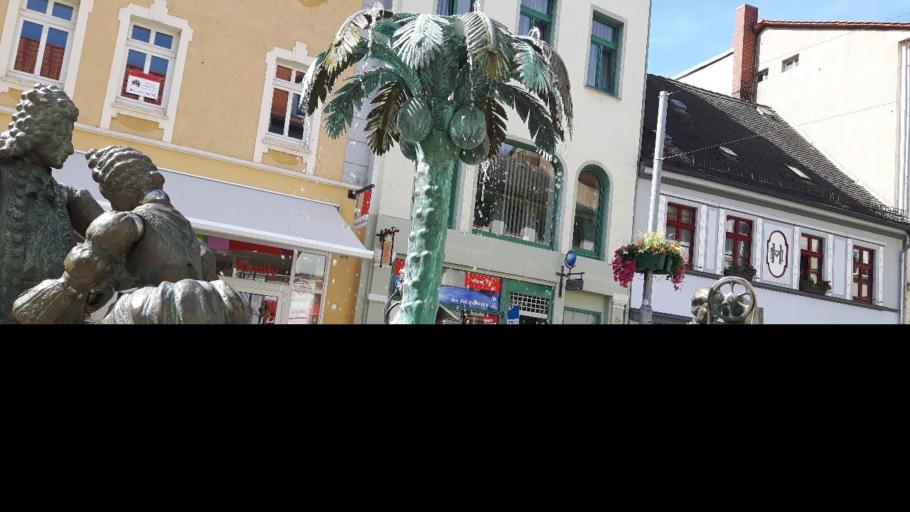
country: DE
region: Saxony-Anhalt
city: Weissenfels
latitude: 51.2012
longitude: 11.9696
